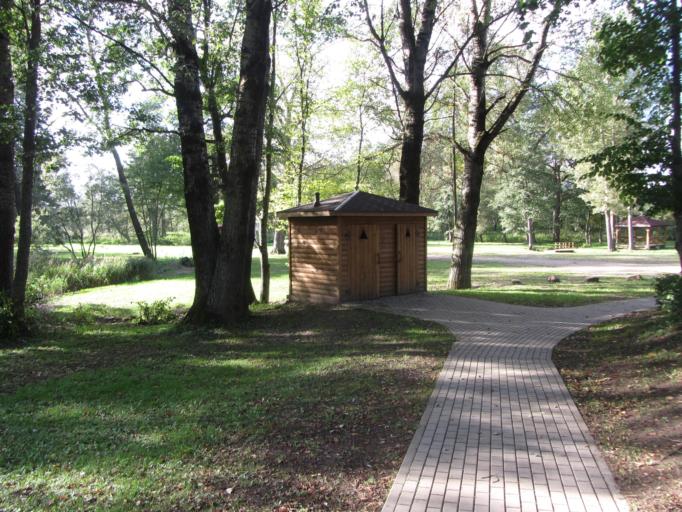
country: LT
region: Panevezys
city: Rokiskis
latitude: 55.9423
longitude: 25.7931
